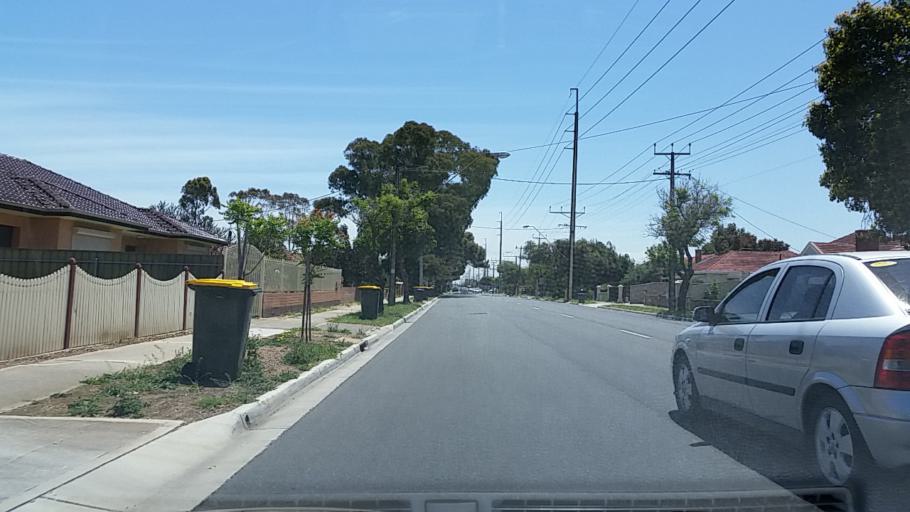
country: AU
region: South Australia
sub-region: Charles Sturt
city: Findon
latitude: -34.8985
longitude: 138.5320
